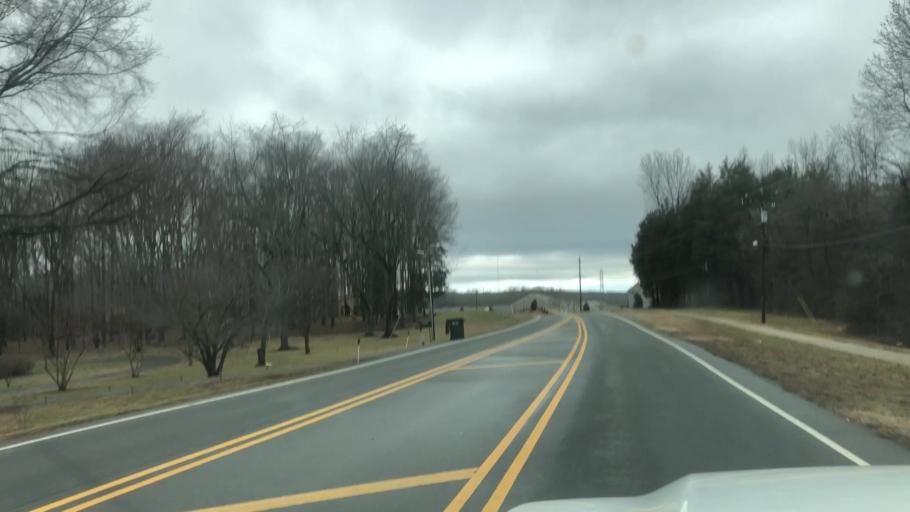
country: US
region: North Carolina
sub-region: Mecklenburg County
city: Mint Hill
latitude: 35.2416
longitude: -80.6757
